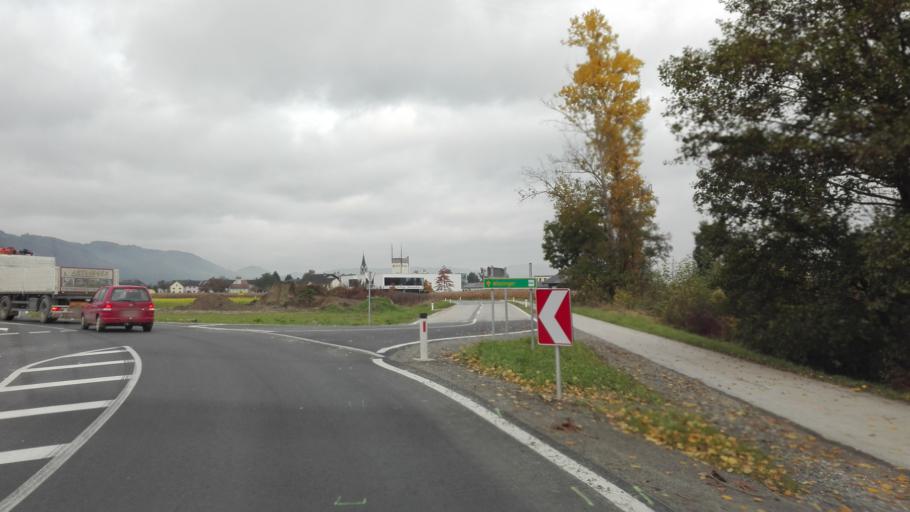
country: AT
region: Upper Austria
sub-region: Politischer Bezirk Urfahr-Umgebung
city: Feldkirchen an der Donau
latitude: 48.3329
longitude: 14.0058
